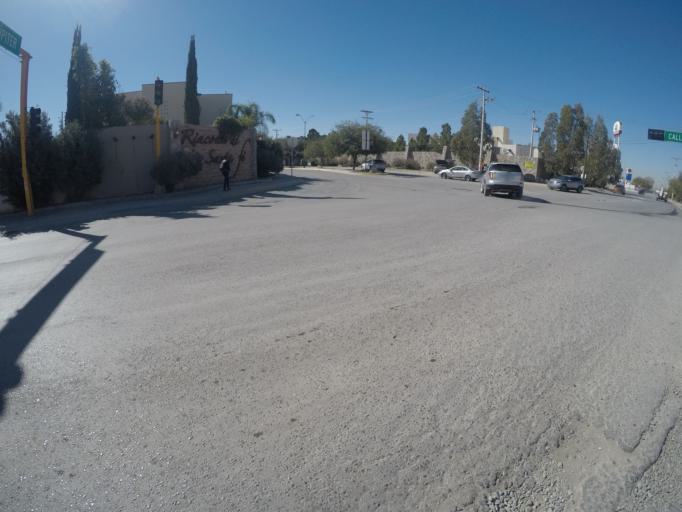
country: US
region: Texas
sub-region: El Paso County
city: Socorro
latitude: 31.6917
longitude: -106.3606
